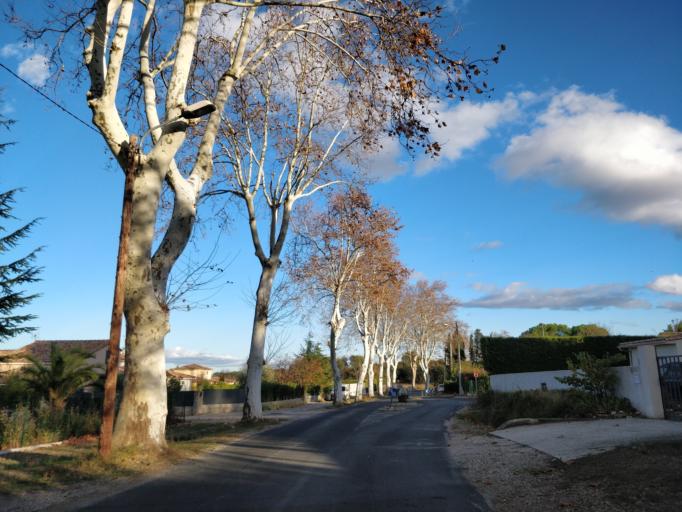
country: FR
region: Languedoc-Roussillon
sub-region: Departement de l'Herault
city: Beaulieu
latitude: 43.7443
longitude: 4.0035
